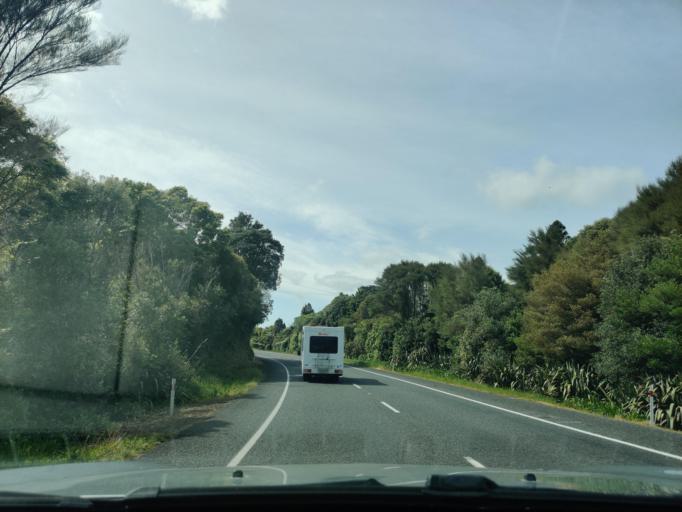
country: NZ
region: Taranaki
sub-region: New Plymouth District
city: New Plymouth
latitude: -39.0883
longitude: 174.0986
